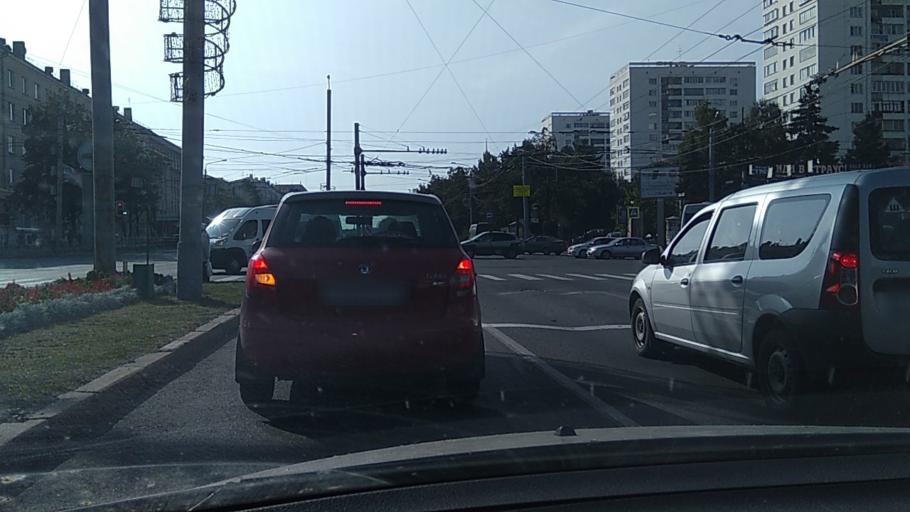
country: RU
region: Chelyabinsk
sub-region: Gorod Chelyabinsk
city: Chelyabinsk
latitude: 55.1598
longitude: 61.3819
